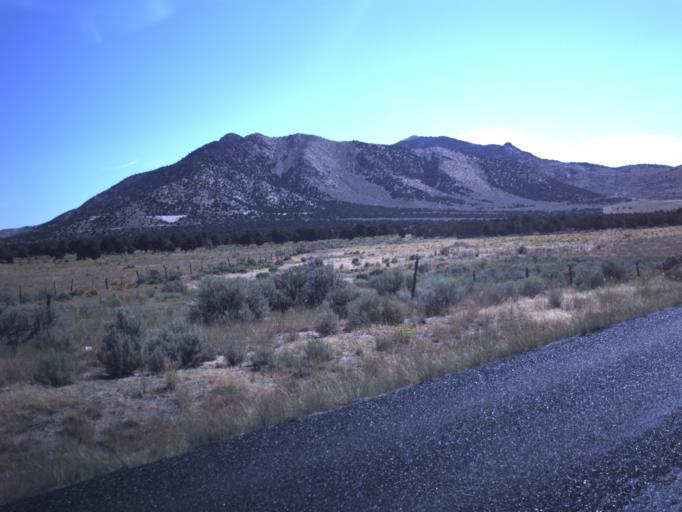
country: US
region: Utah
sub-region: Utah County
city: Genola
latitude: 39.9334
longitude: -112.1723
